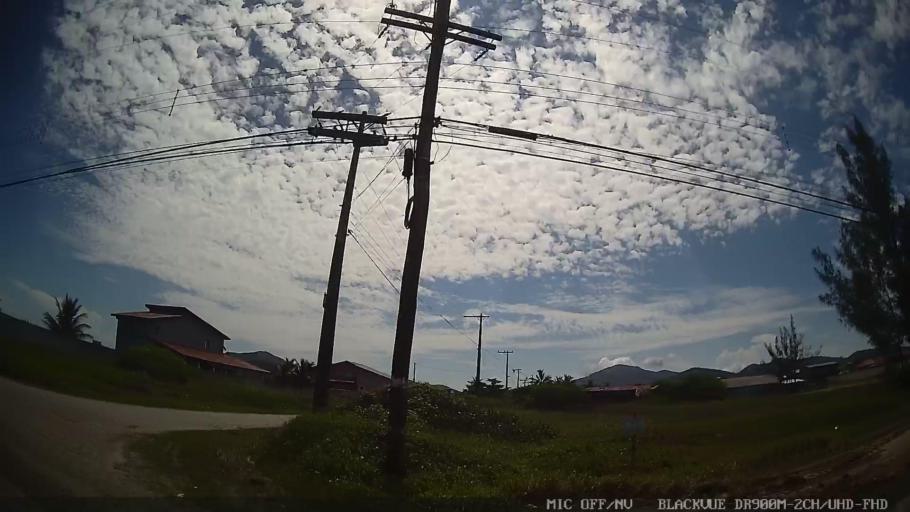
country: BR
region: Sao Paulo
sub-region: Iguape
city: Iguape
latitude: -24.7240
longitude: -47.5062
